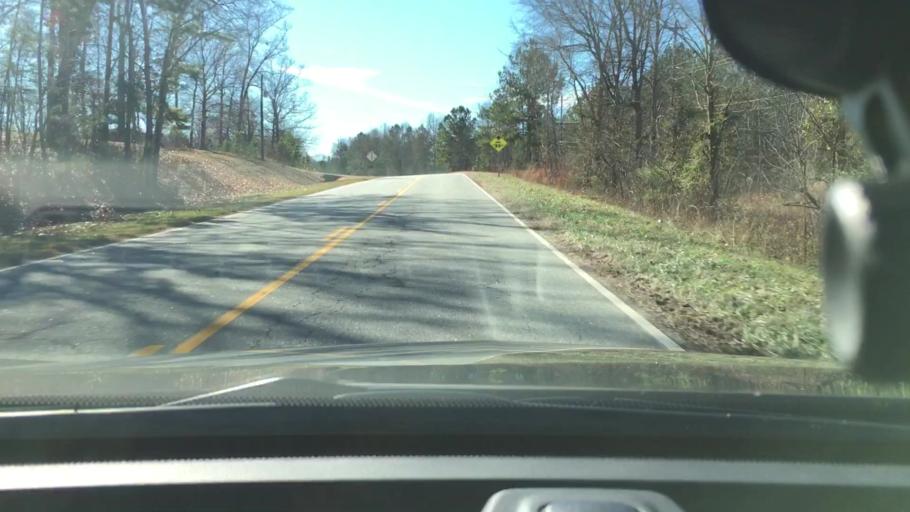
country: US
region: South Carolina
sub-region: Cherokee County
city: Gaffney
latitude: 35.0464
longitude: -81.6746
